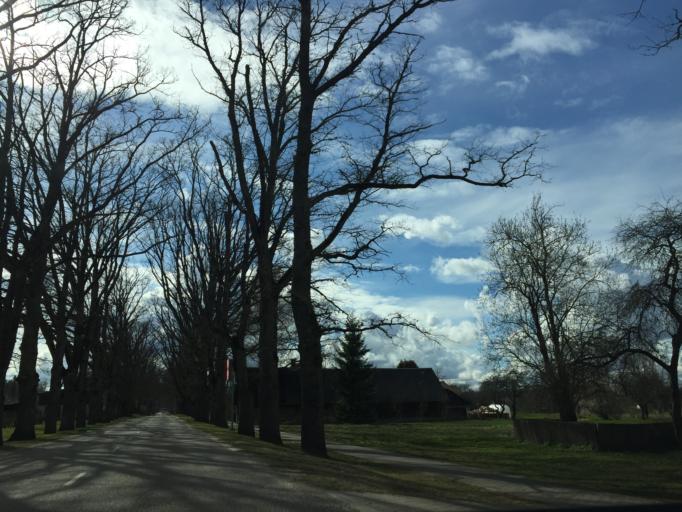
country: LV
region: Burtnieki
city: Matisi
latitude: 57.5973
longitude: 25.0908
